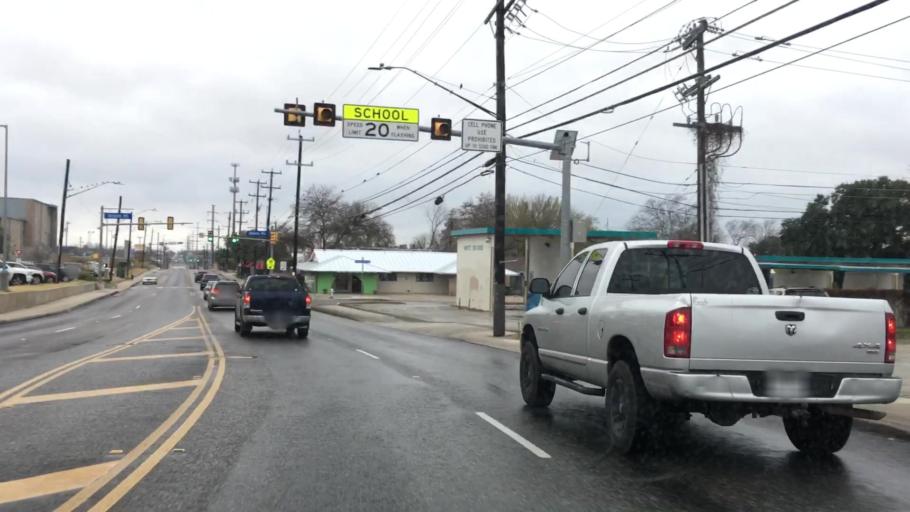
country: US
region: Texas
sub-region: Bexar County
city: Castle Hills
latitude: 29.5023
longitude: -98.5078
